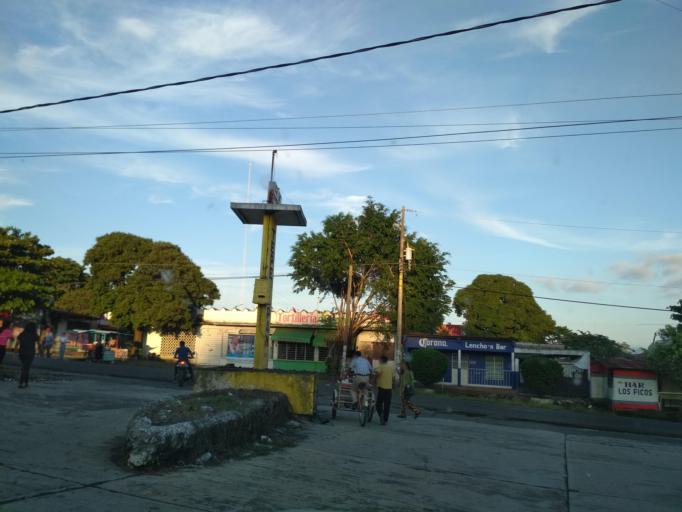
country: MX
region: Veracruz
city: Catemaco
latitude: 18.4189
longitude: -95.1192
